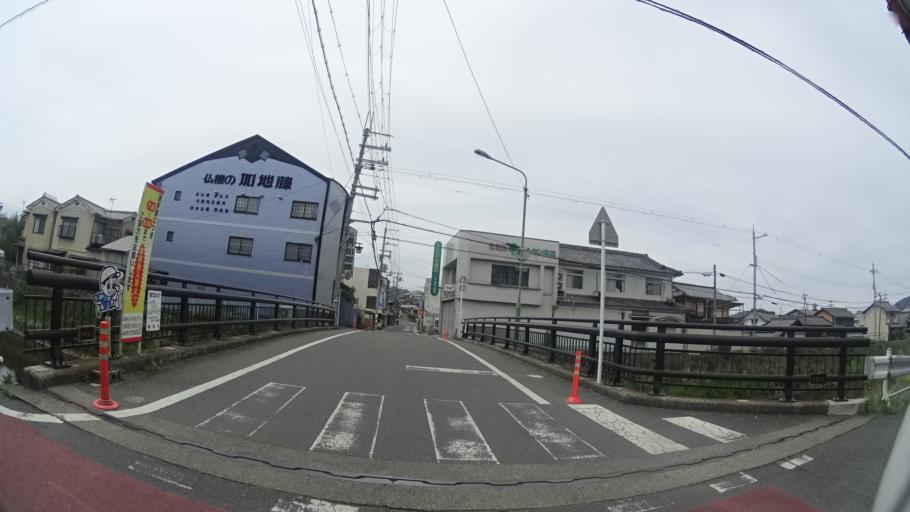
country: JP
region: Kyoto
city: Kameoka
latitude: 35.0179
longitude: 135.5738
